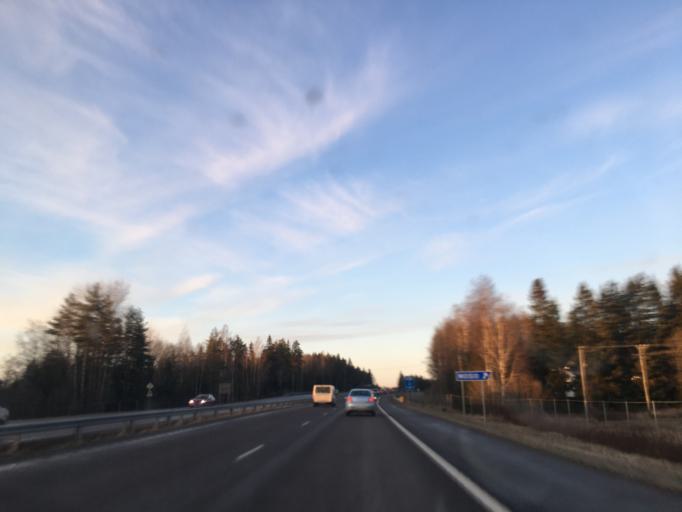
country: FI
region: Varsinais-Suomi
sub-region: Turku
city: Vahto
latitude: 60.5280
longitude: 22.3062
